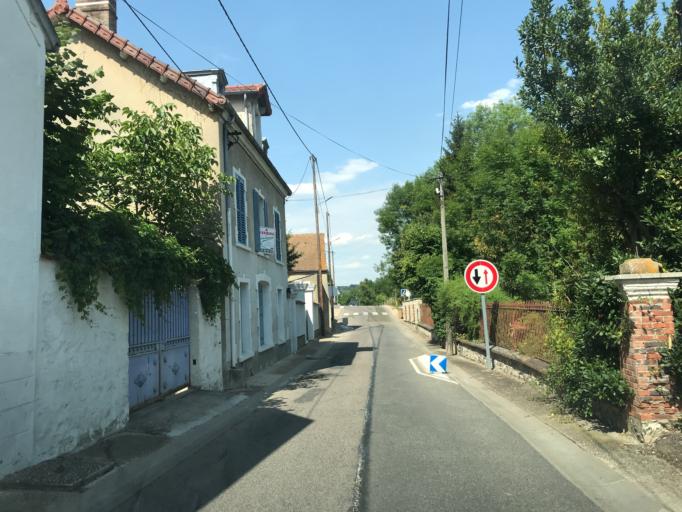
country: FR
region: Ile-de-France
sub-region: Departement des Yvelines
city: Freneuse
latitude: 49.0595
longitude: 1.5987
